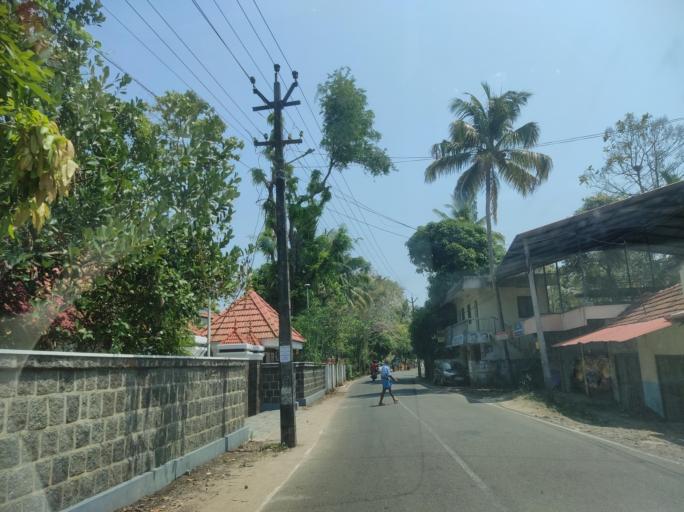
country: IN
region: Kerala
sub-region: Alappuzha
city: Kutiatodu
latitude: 9.7974
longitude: 76.3019
